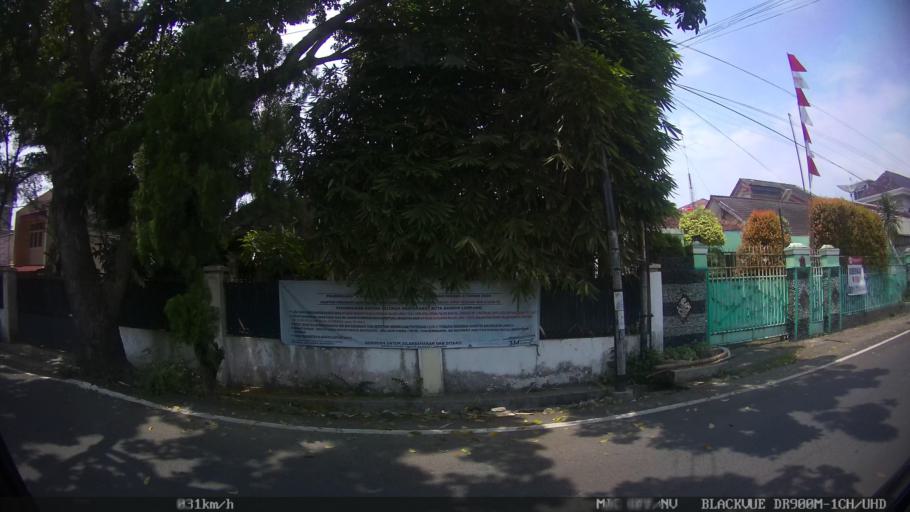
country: ID
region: Lampung
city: Bandarlampung
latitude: -5.4304
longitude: 105.2727
